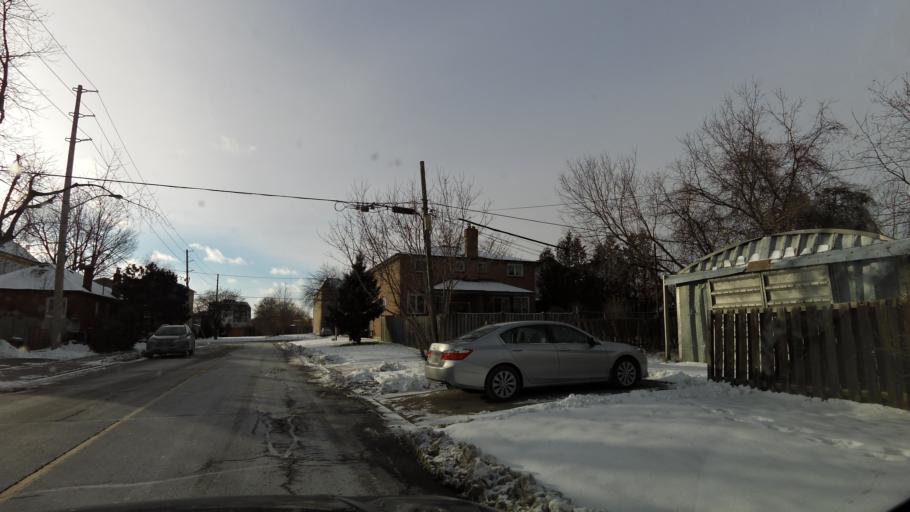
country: CA
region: Ontario
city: Etobicoke
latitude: 43.5977
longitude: -79.5312
